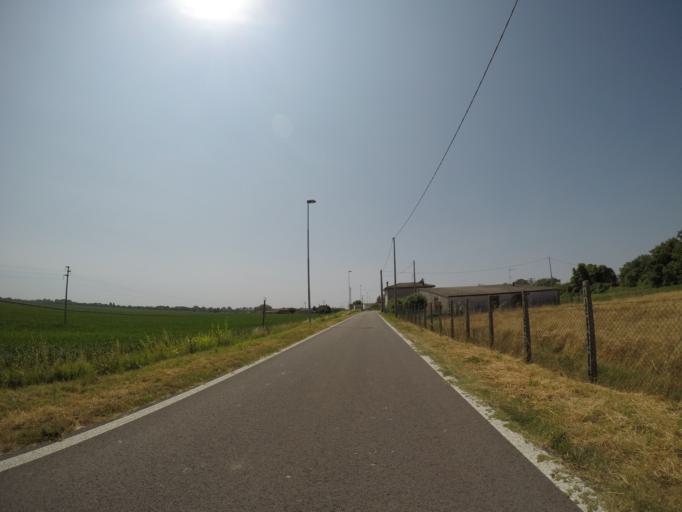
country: IT
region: Veneto
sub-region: Provincia di Rovigo
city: Fratta Polesine
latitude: 45.0149
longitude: 11.6412
